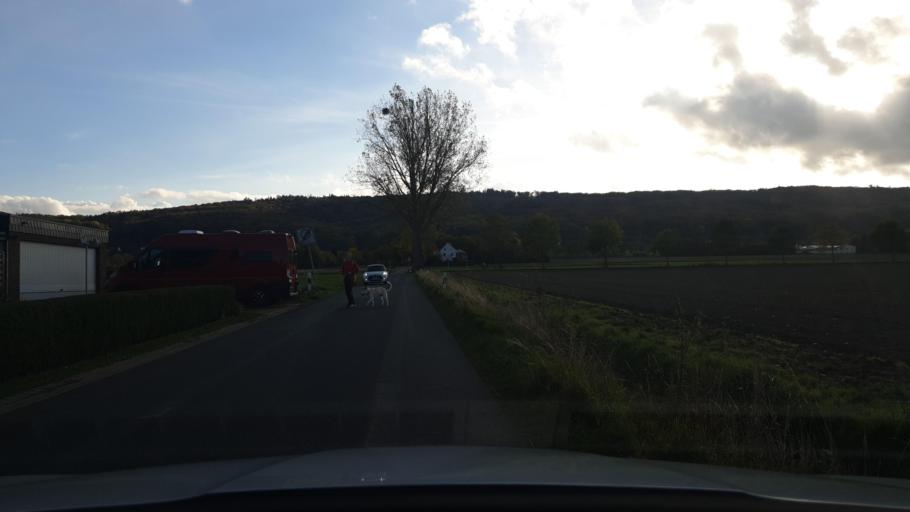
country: DE
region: North Rhine-Westphalia
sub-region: Regierungsbezirk Detmold
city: Minden
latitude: 52.2675
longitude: 8.8594
